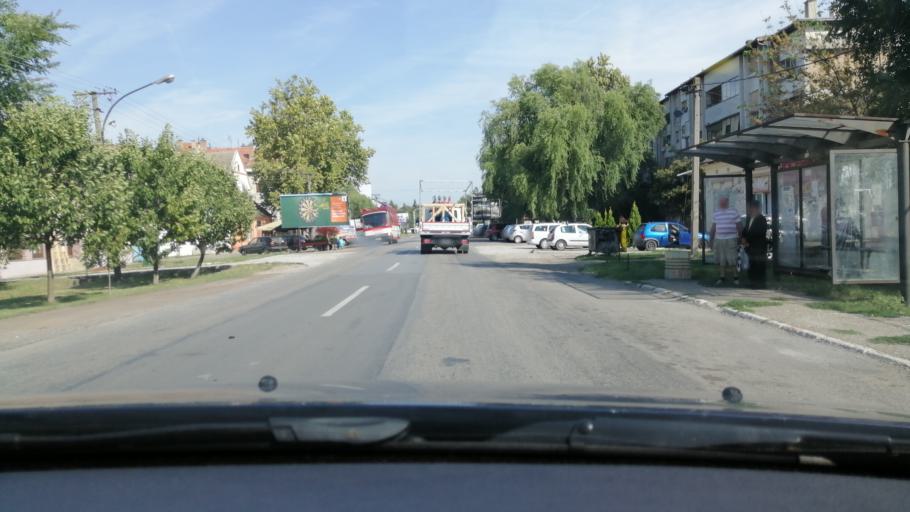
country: RS
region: Autonomna Pokrajina Vojvodina
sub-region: Juznobanatski Okrug
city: Kovacica
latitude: 45.1108
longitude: 20.6187
